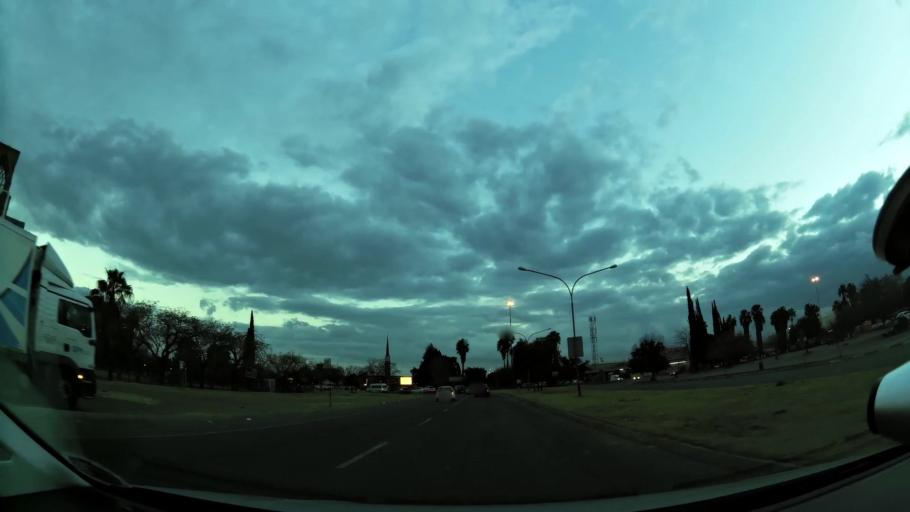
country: ZA
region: Orange Free State
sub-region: Lejweleputswa District Municipality
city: Welkom
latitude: -27.9810
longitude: 26.7427
